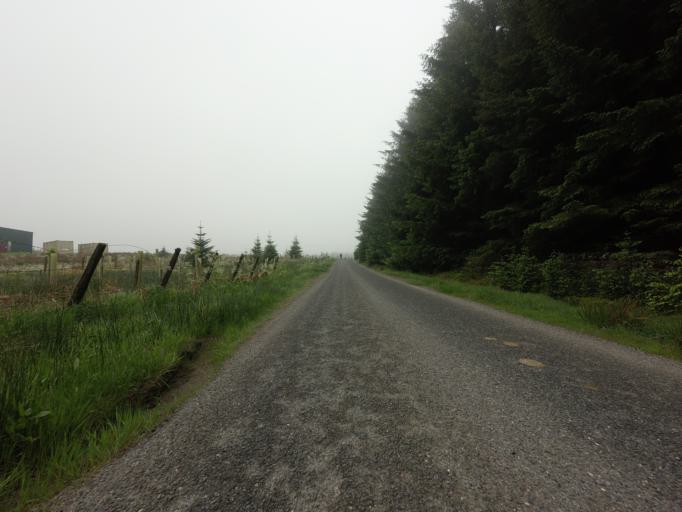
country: GB
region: Scotland
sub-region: Perth and Kinross
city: Kinross
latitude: 56.1493
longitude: -3.4527
